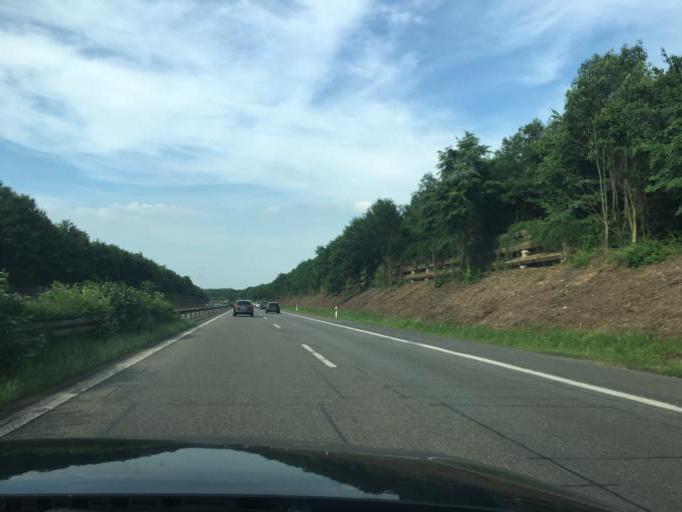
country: DE
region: North Rhine-Westphalia
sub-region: Regierungsbezirk Dusseldorf
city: Hochfeld
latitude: 51.3582
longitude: 6.7632
